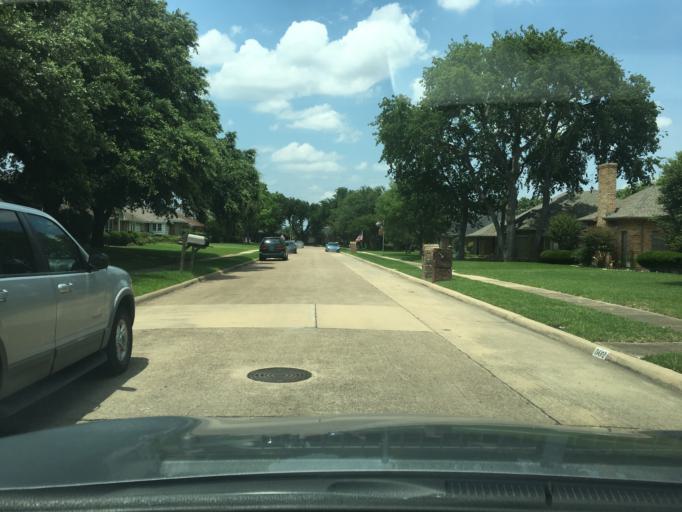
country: US
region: Texas
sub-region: Dallas County
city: Richardson
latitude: 32.9547
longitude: -96.6992
